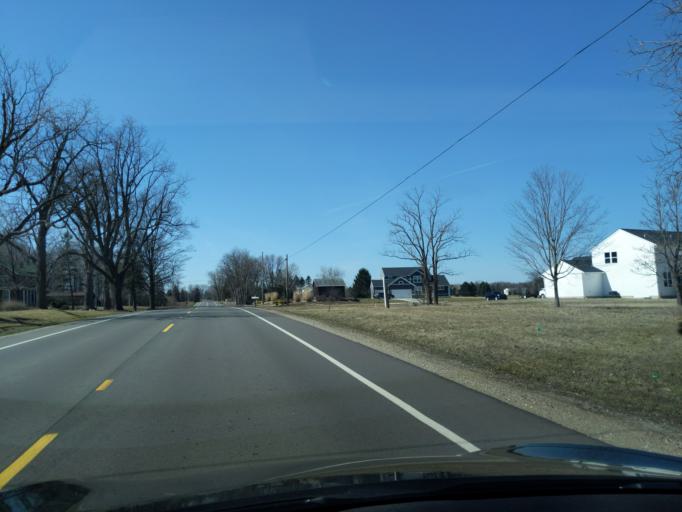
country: US
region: Michigan
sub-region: Eaton County
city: Grand Ledge
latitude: 42.7264
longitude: -84.7110
